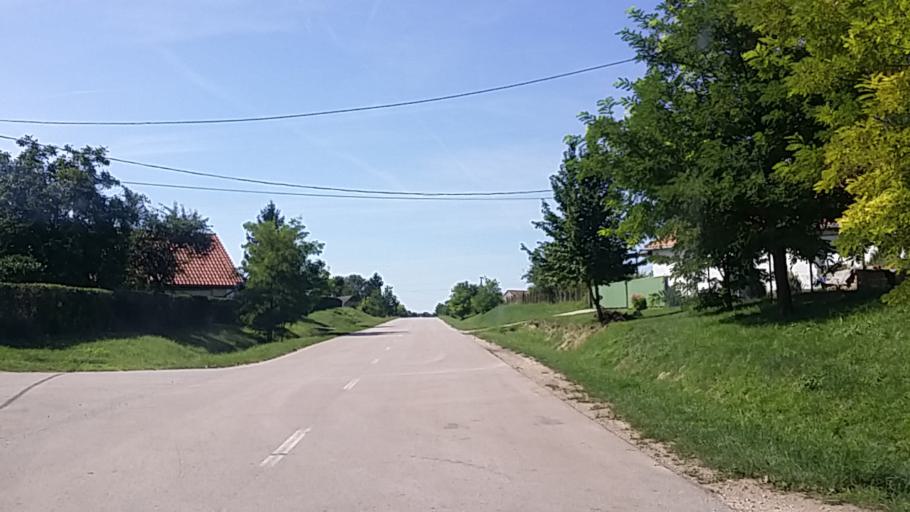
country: HU
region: Fejer
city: Deg
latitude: 46.8813
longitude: 18.4464
